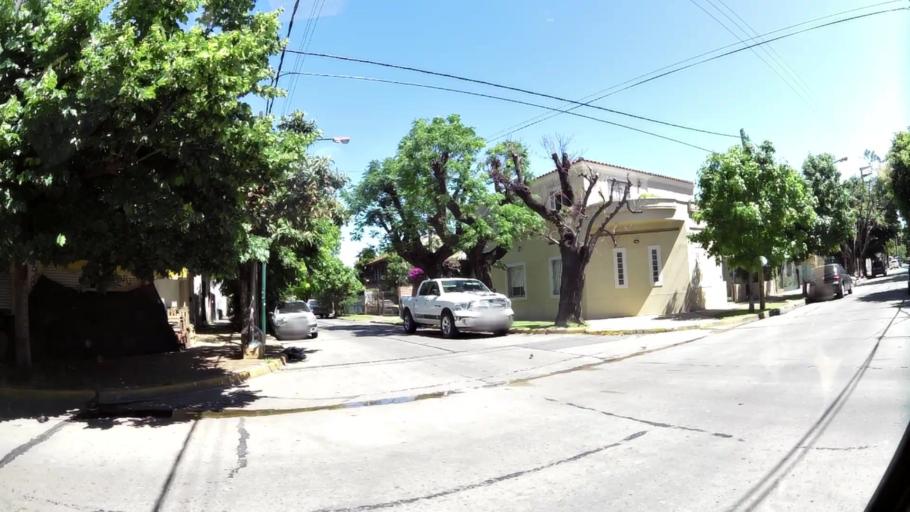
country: AR
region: Buenos Aires
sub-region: Partido de San Isidro
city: San Isidro
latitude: -34.4863
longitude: -58.5120
